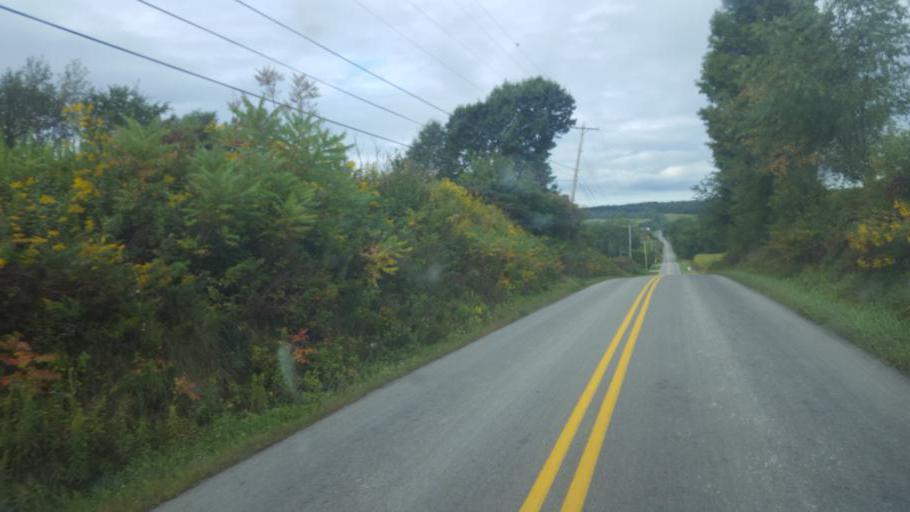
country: US
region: Pennsylvania
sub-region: Mercer County
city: Greenville
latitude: 41.5052
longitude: -80.3505
